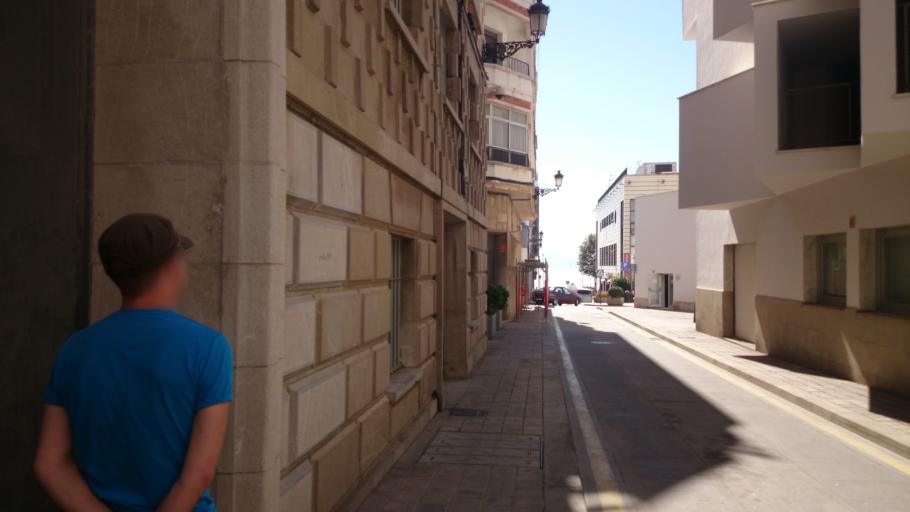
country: ES
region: Ceuta
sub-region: Ceuta
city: Ceuta
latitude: 35.8870
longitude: -5.3103
